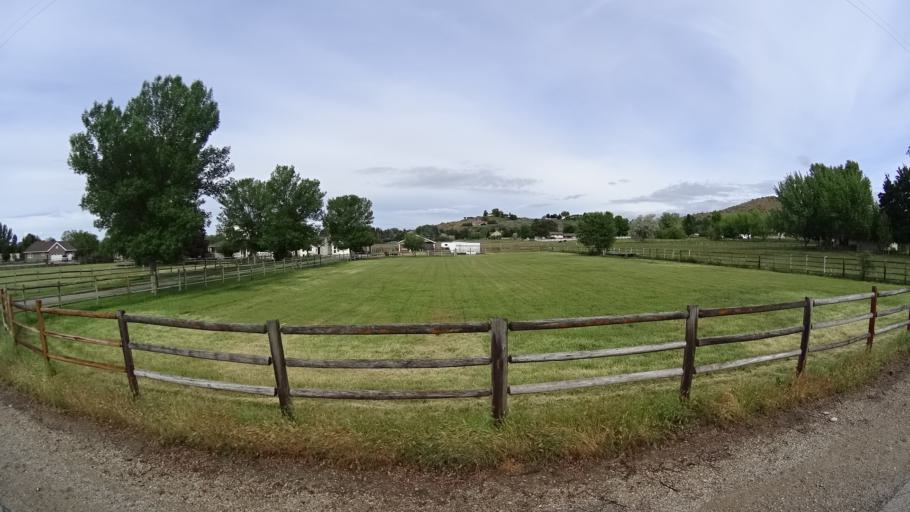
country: US
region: Idaho
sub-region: Ada County
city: Eagle
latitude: 43.7269
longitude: -116.3192
